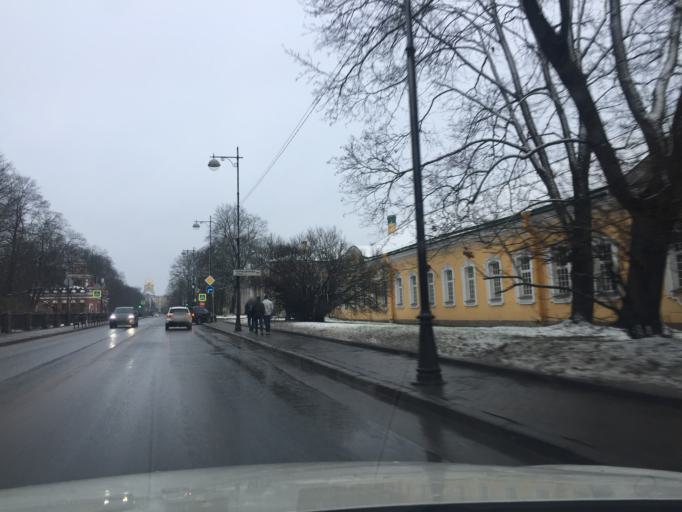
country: RU
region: St.-Petersburg
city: Pushkin
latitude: 59.7140
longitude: 30.4075
